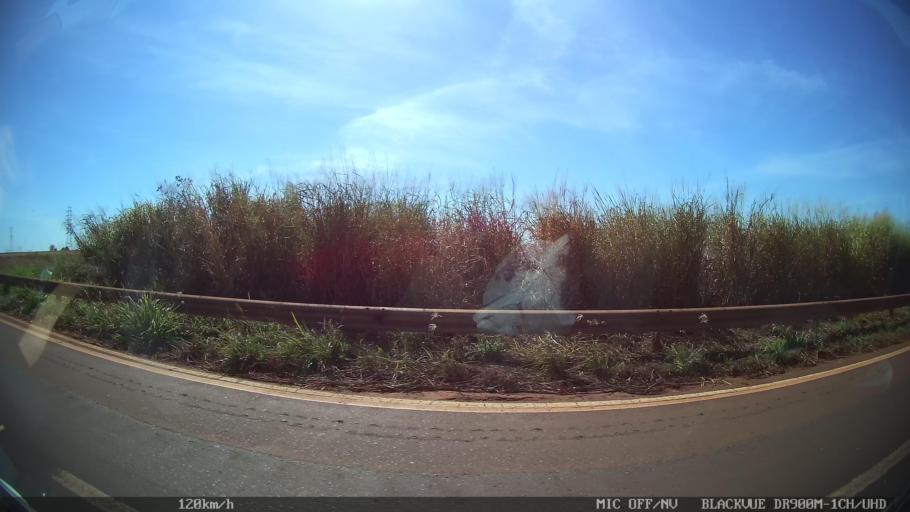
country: BR
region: Sao Paulo
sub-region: Guaira
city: Guaira
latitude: -20.4457
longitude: -48.4119
